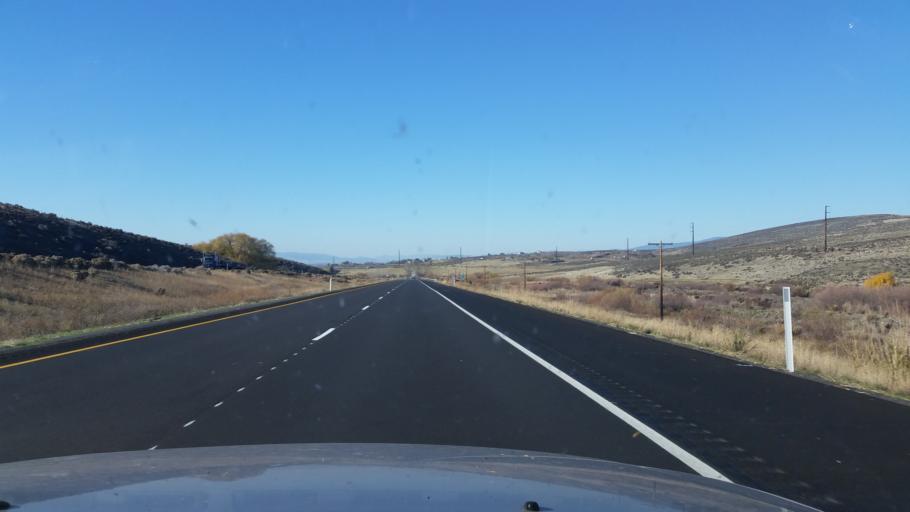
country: US
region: Washington
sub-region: Kittitas County
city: Kittitas
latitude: 46.9667
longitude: -120.3387
